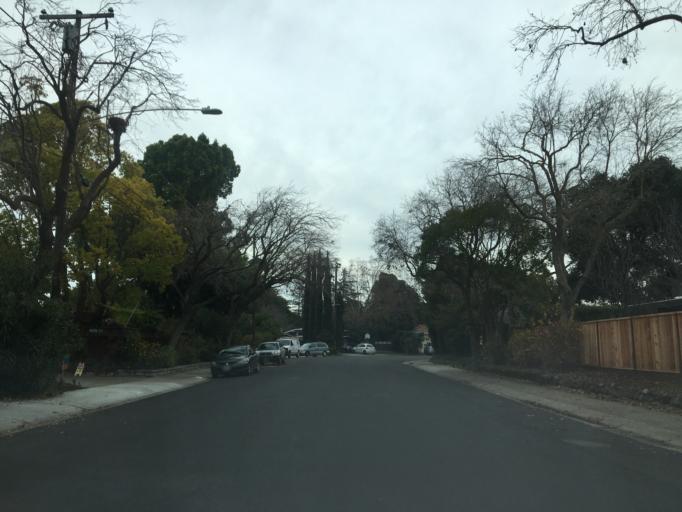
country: US
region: California
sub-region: Santa Clara County
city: Los Altos
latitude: 37.4130
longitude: -122.1171
